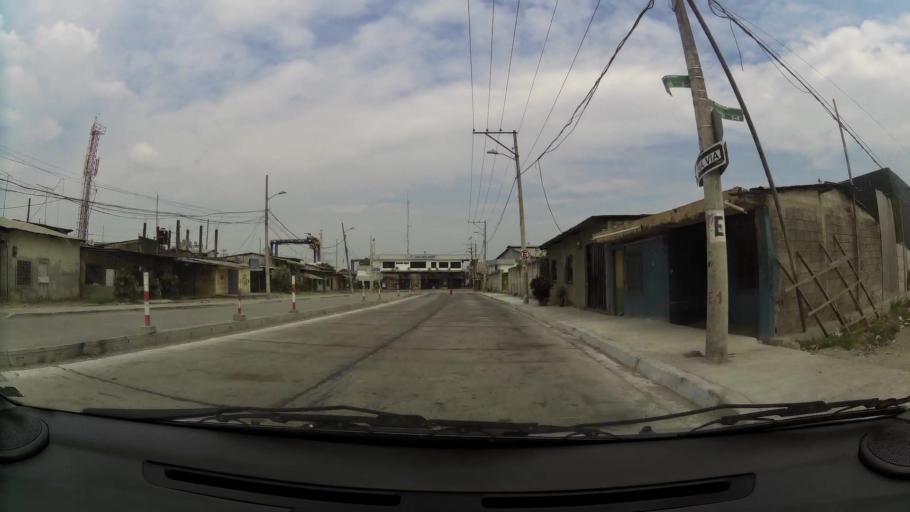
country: EC
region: Guayas
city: Guayaquil
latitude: -2.2494
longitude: -79.9254
